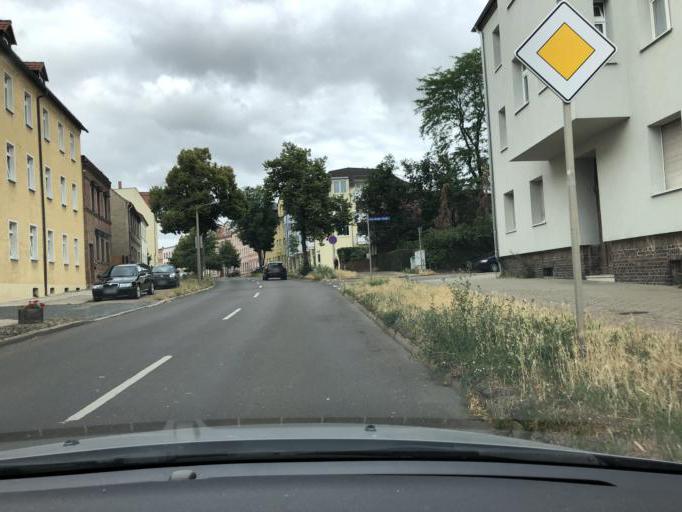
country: DE
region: Saxony-Anhalt
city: Schkopau
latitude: 51.4277
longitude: 11.9821
